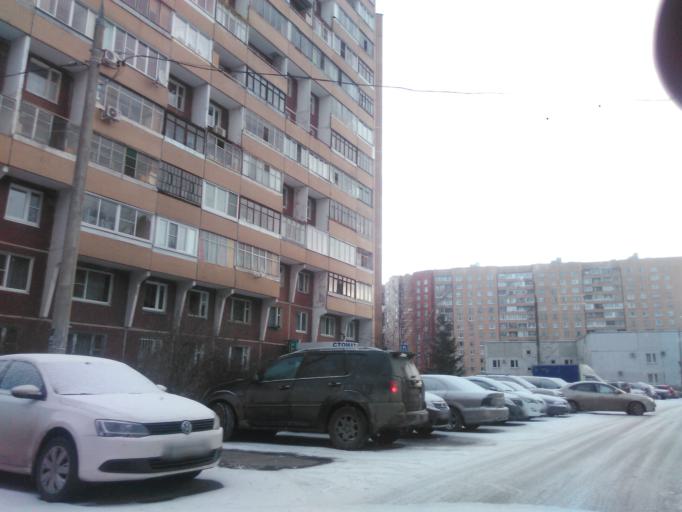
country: RU
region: Moscow
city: Zelenograd
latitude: 55.9962
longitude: 37.1745
